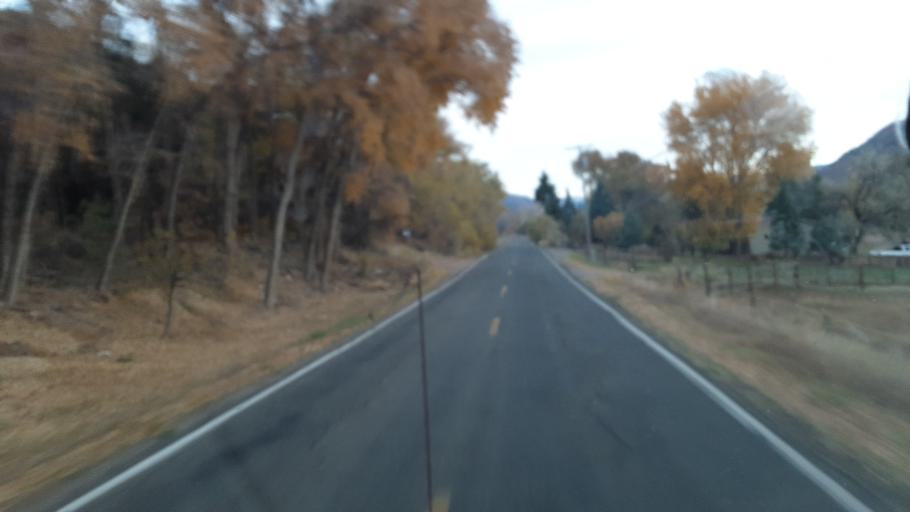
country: US
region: Colorado
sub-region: La Plata County
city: Durango
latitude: 37.3521
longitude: -107.8567
